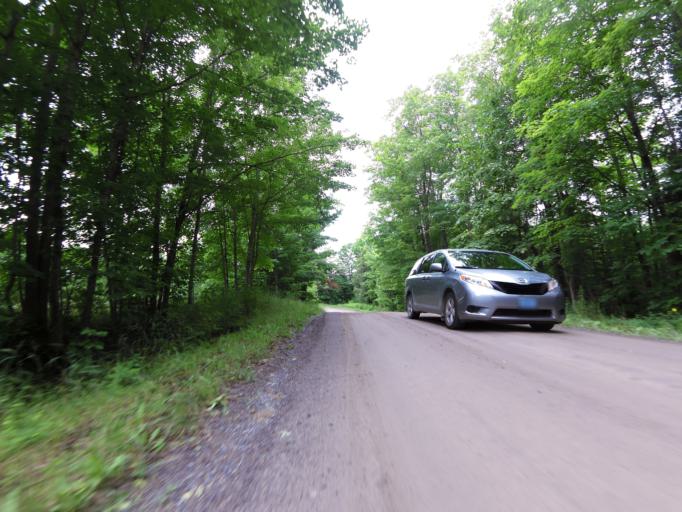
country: CA
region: Ontario
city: Kingston
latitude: 44.5532
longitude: -76.6262
